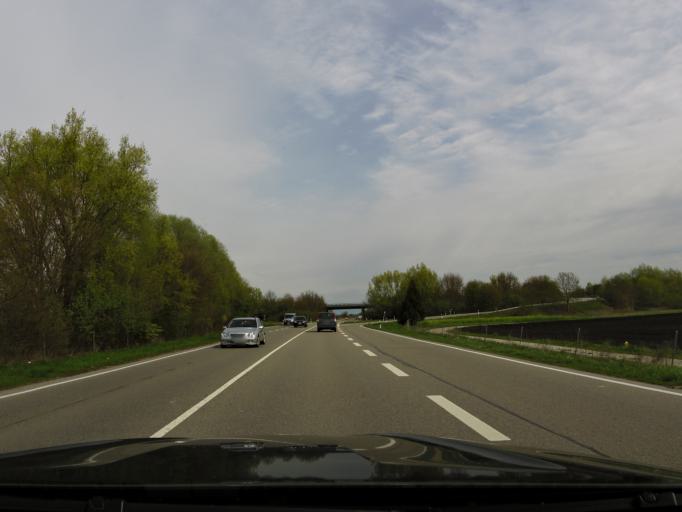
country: DE
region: Bavaria
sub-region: Upper Bavaria
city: Eitting
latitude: 48.3689
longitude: 11.8536
